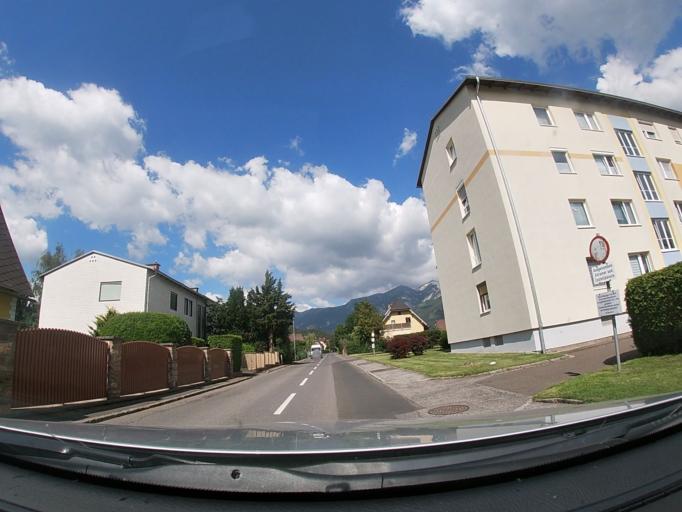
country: AT
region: Styria
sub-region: Politischer Bezirk Leoben
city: Trofaiach
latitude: 47.4249
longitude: 14.9924
